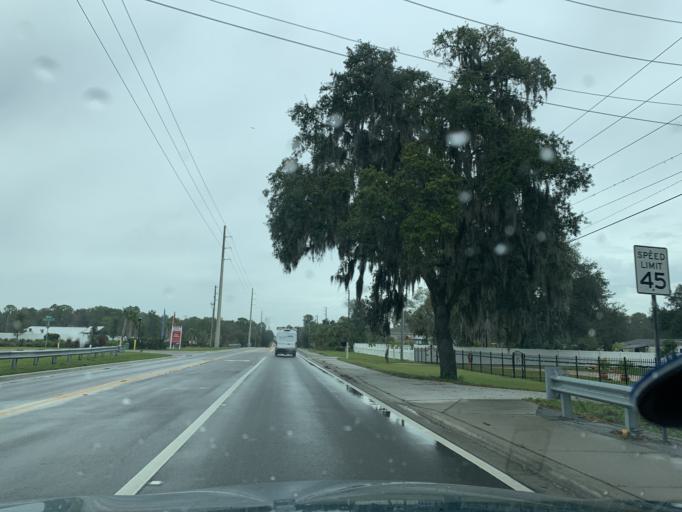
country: US
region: Florida
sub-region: Pasco County
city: Wesley Chapel
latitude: 28.2588
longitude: -82.3201
